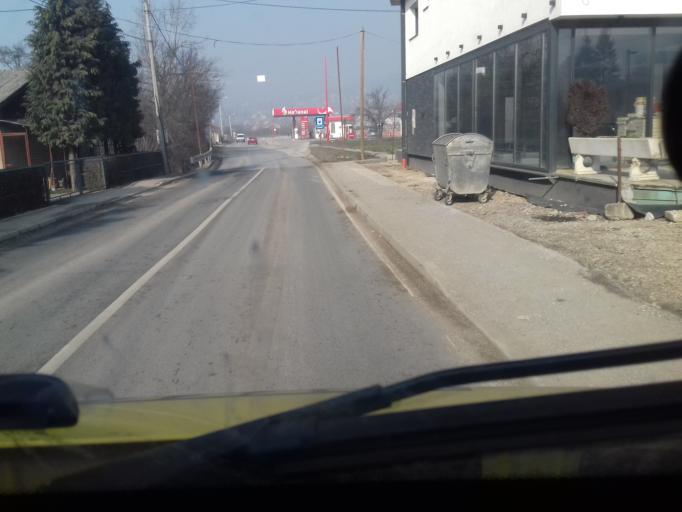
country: BA
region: Federation of Bosnia and Herzegovina
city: Ilijas
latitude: 43.9621
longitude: 18.2640
